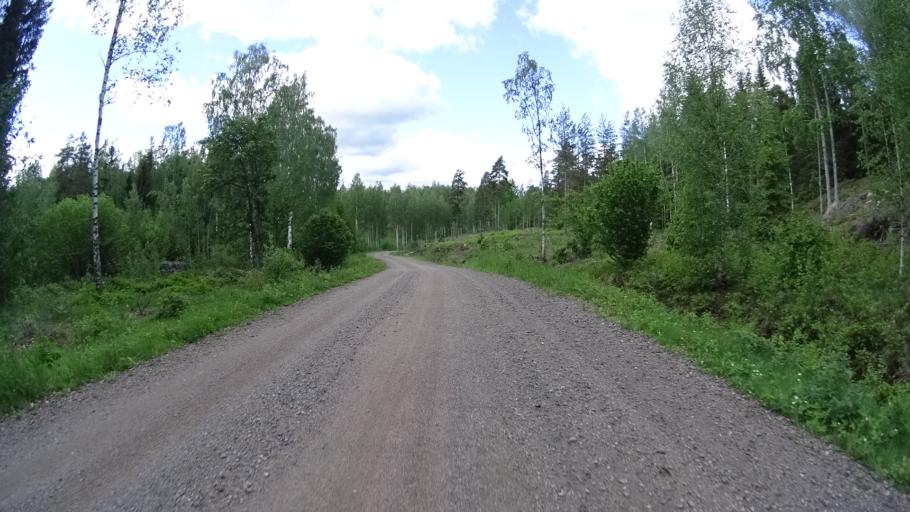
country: FI
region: Uusimaa
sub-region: Raaseporin
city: Karis
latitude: 60.1395
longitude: 23.6233
